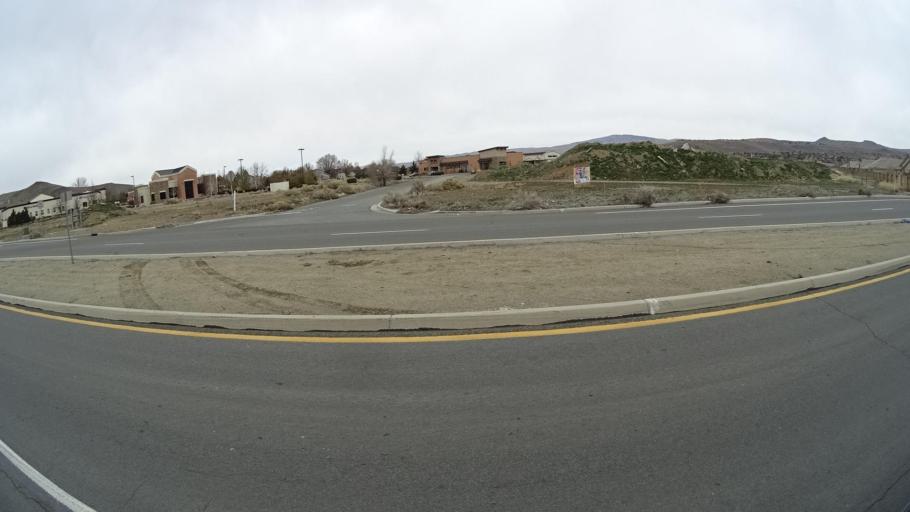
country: US
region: Nevada
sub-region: Washoe County
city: Sun Valley
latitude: 39.5836
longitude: -119.7382
